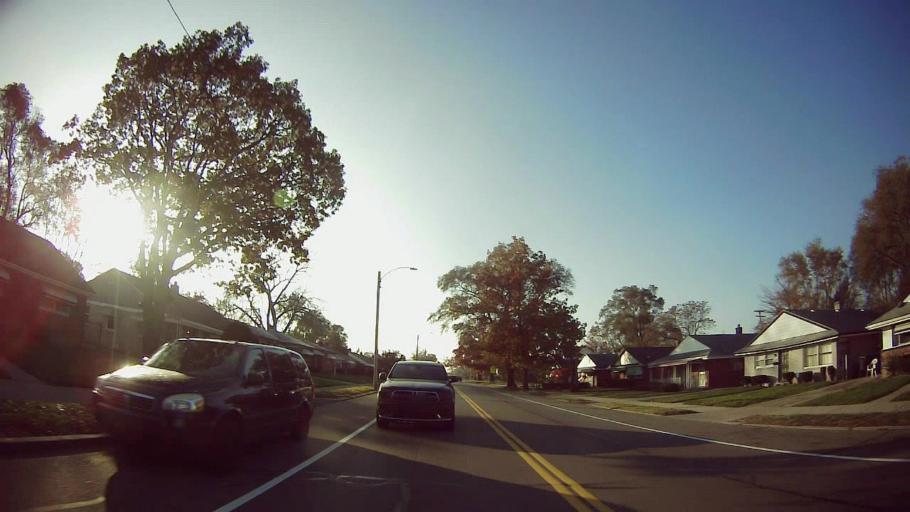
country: US
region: Michigan
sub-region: Oakland County
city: Oak Park
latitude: 42.4394
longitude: -83.1612
